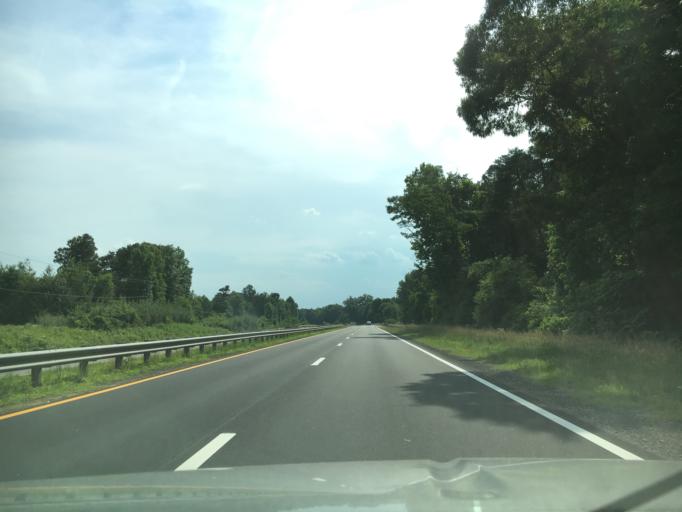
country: US
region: Virginia
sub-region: Halifax County
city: Halifax
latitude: 36.8157
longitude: -78.7444
